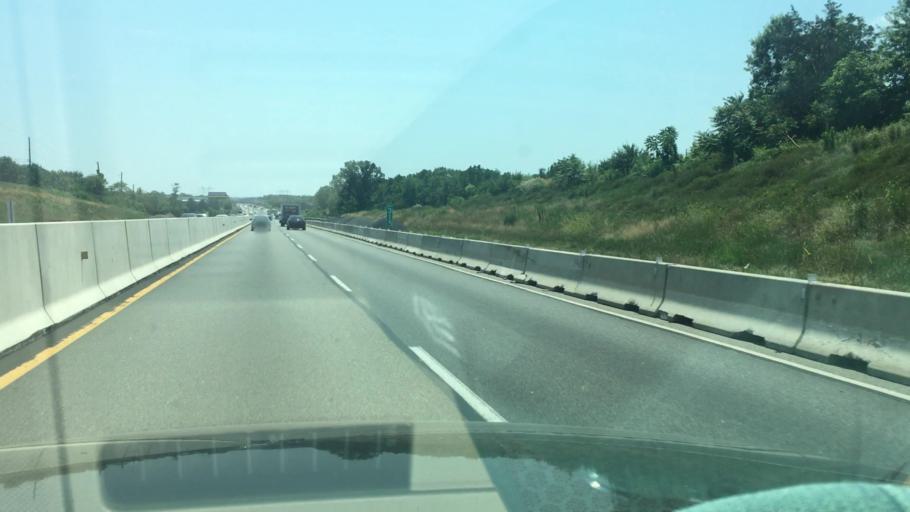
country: US
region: Pennsylvania
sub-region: Montgomery County
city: Kulpsville
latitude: 40.2678
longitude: -75.3554
